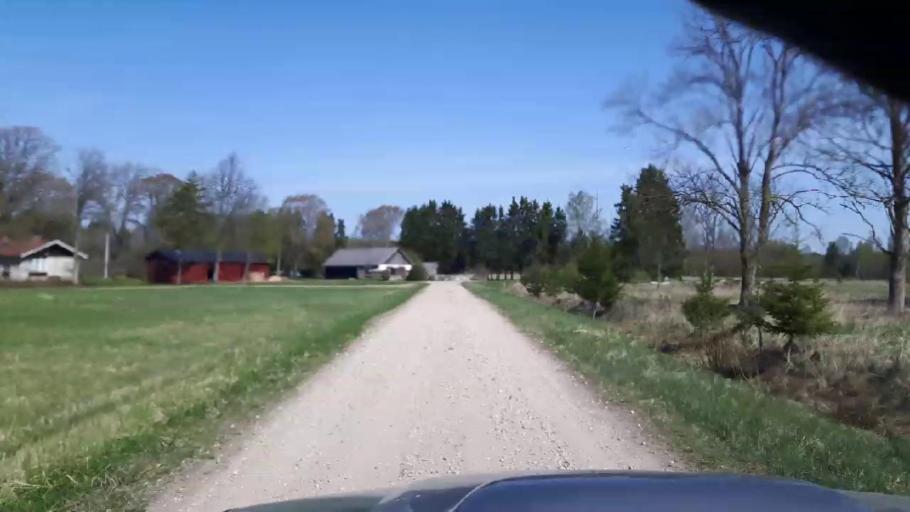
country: EE
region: Paernumaa
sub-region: Tootsi vald
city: Tootsi
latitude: 58.4963
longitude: 24.9291
